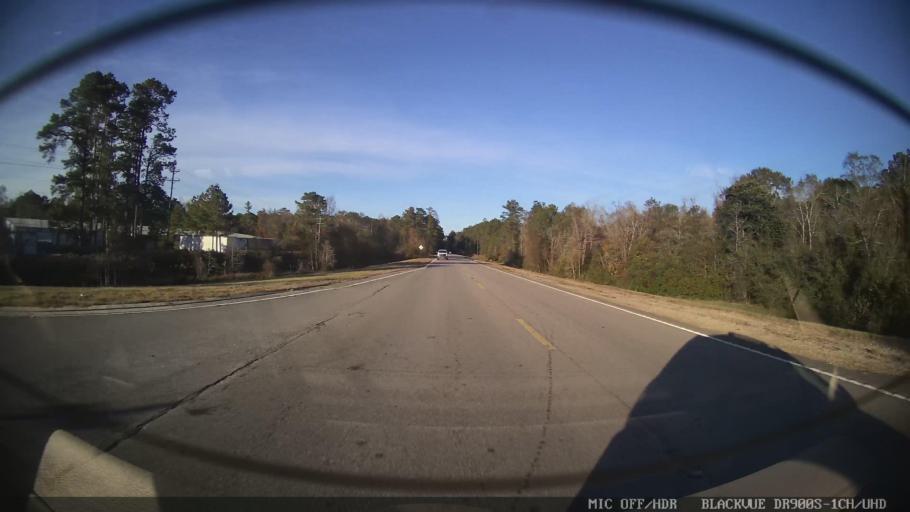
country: US
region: Mississippi
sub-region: Lamar County
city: Purvis
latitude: 31.0727
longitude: -89.4207
